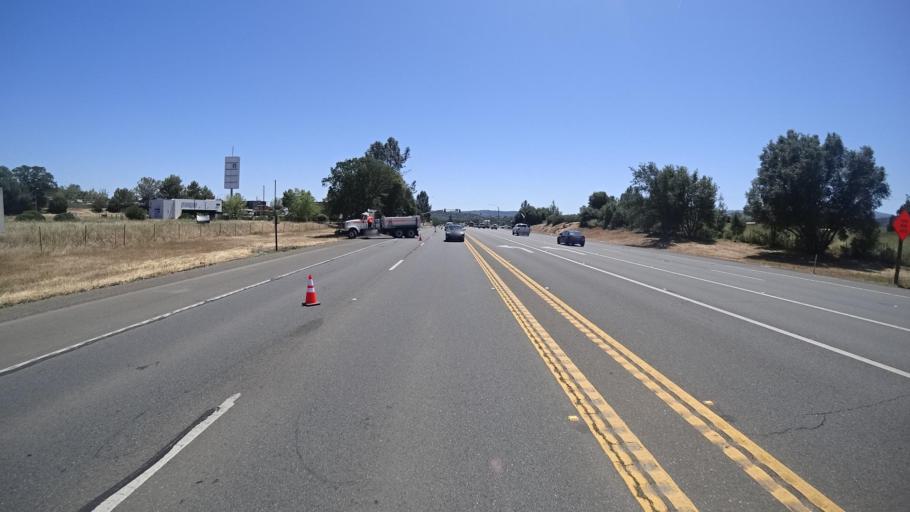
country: US
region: California
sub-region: Lake County
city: Lower Lake
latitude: 38.9313
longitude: -122.6195
